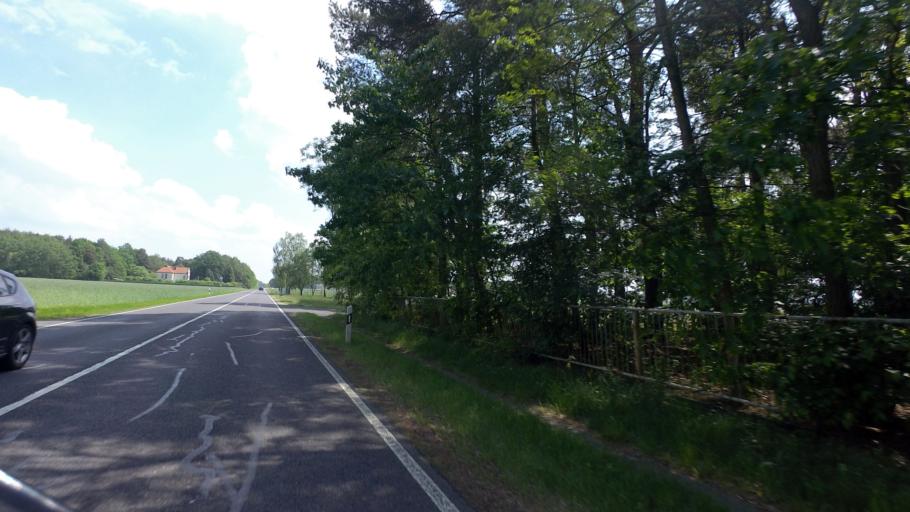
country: DE
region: Saxony
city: Schleife
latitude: 51.5486
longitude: 14.5224
